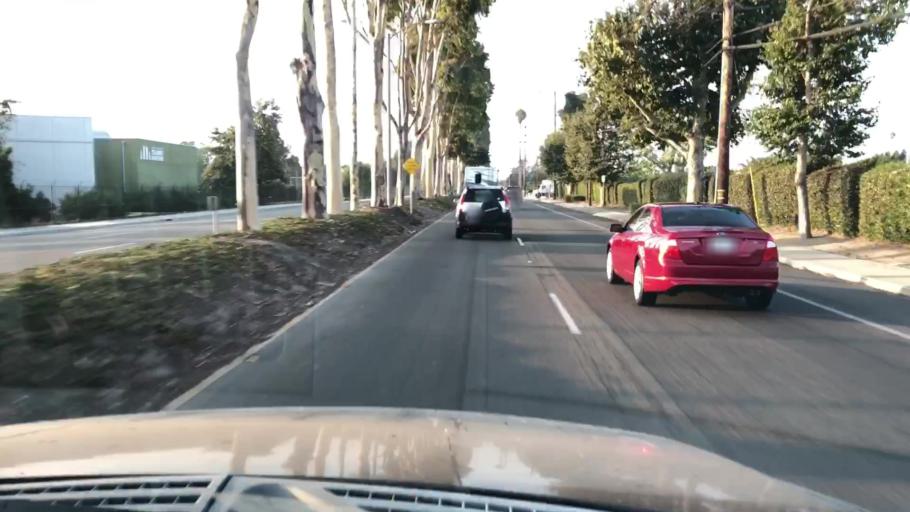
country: US
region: California
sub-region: Ventura County
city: Port Hueneme
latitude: 34.1692
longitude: -119.1950
